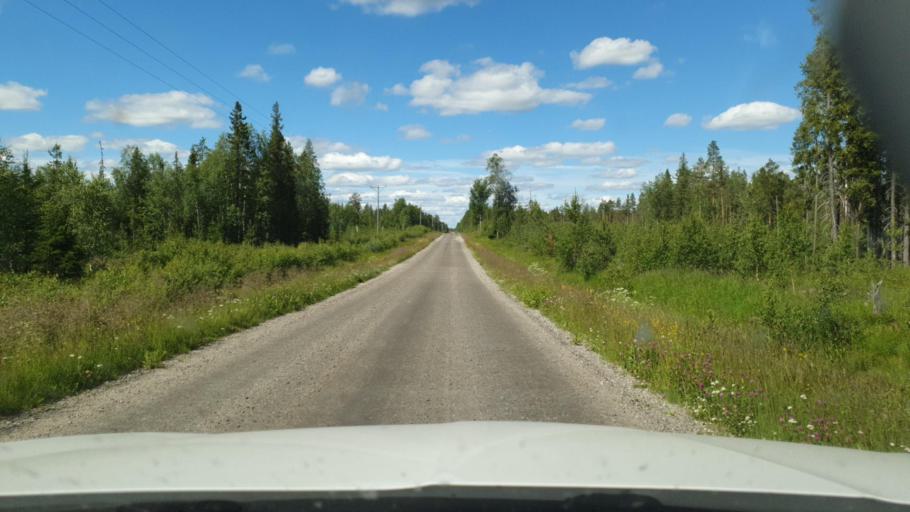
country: SE
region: Vaesterbotten
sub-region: Skelleftea Kommun
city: Backa
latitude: 65.1636
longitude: 21.1395
